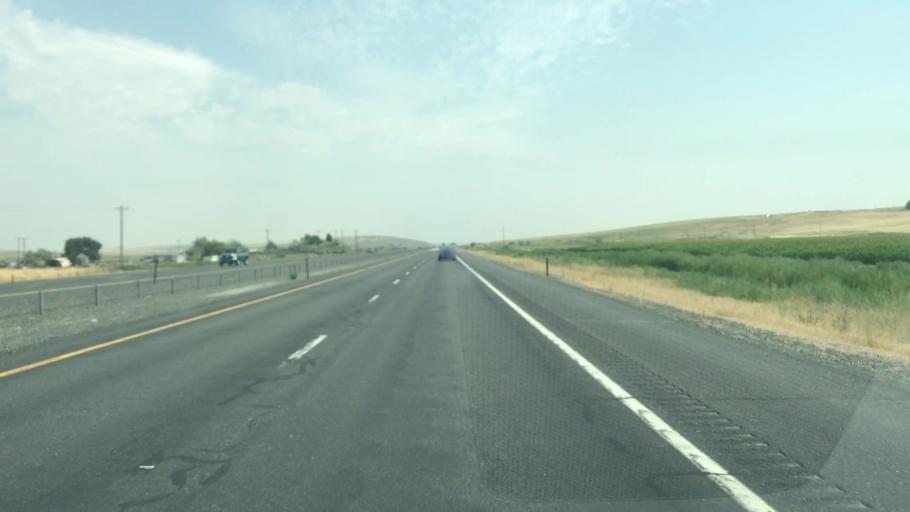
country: US
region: Washington
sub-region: Grant County
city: Warden
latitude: 47.0852
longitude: -119.0281
